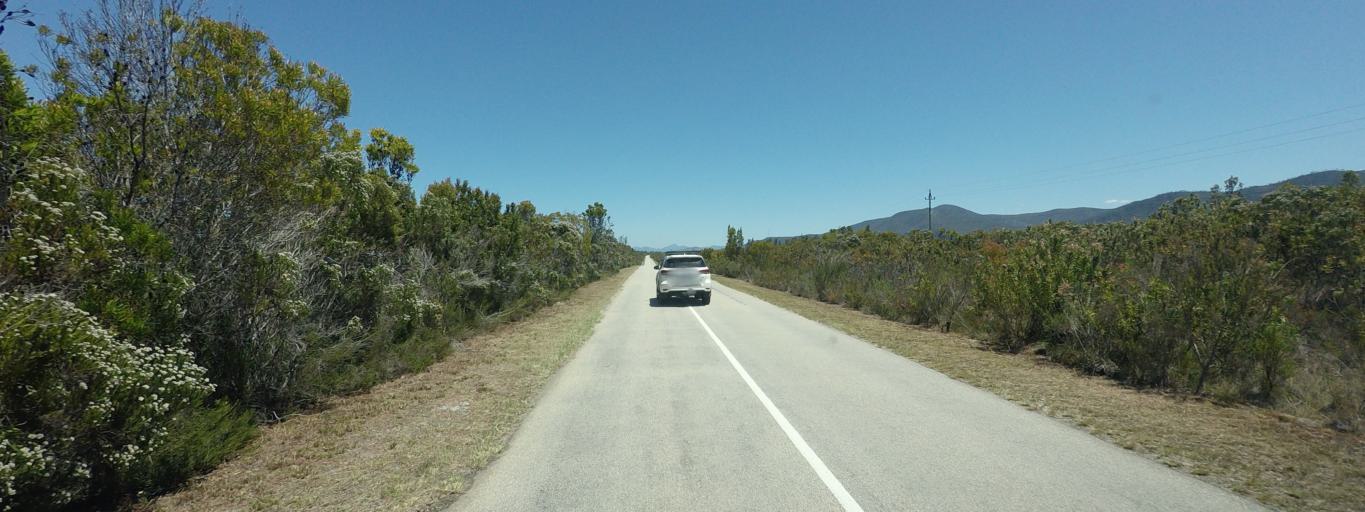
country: ZA
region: Western Cape
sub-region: Eden District Municipality
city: Plettenberg Bay
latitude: -33.9602
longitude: 23.5281
